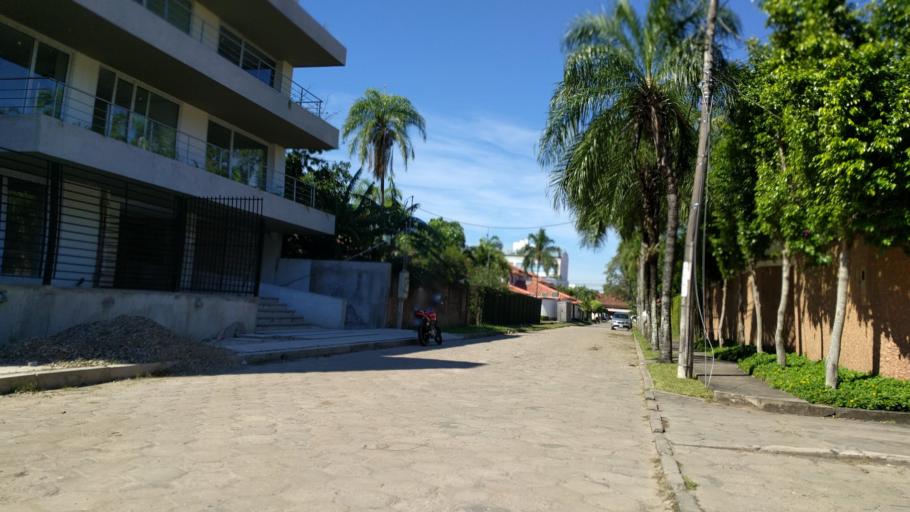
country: BO
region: Santa Cruz
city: Santa Cruz de la Sierra
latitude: -17.8032
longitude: -63.2080
